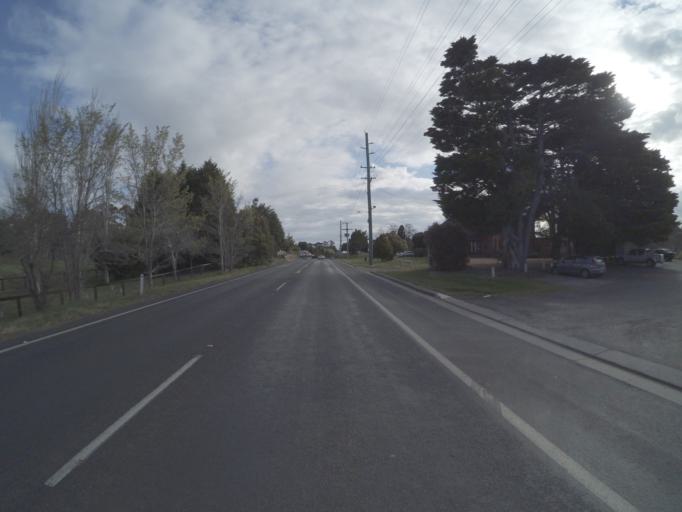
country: AU
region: New South Wales
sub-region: Wingecarribee
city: Moss Vale
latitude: -34.5701
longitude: 150.3186
